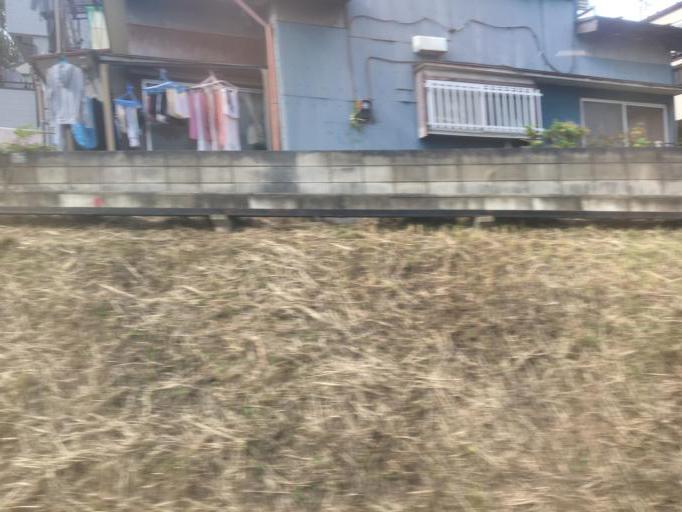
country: JP
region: Saitama
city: Sayama
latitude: 35.8322
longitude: 139.4101
